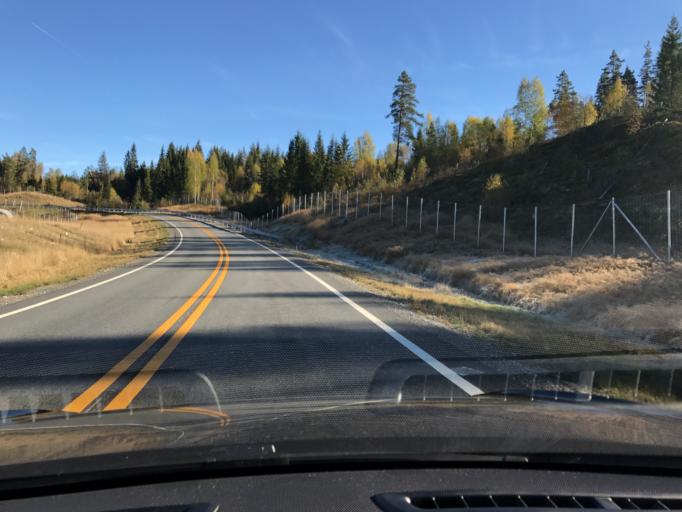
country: NO
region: Buskerud
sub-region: Krodsherad
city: Noresund
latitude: 60.2660
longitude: 9.7921
